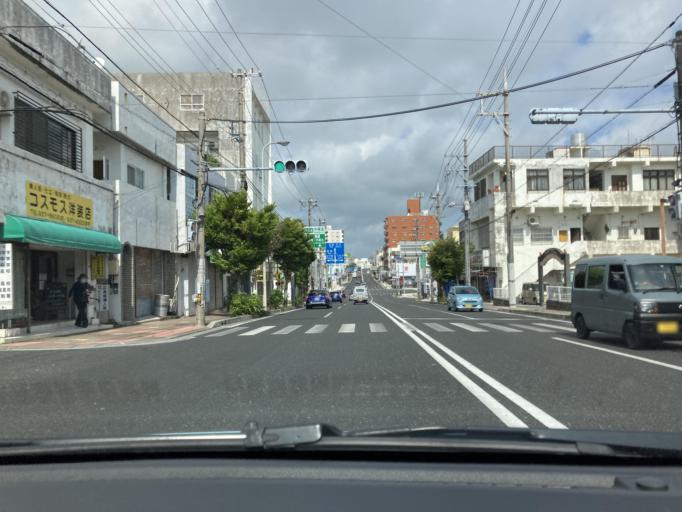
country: JP
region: Okinawa
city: Okinawa
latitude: 26.3381
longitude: 127.8160
